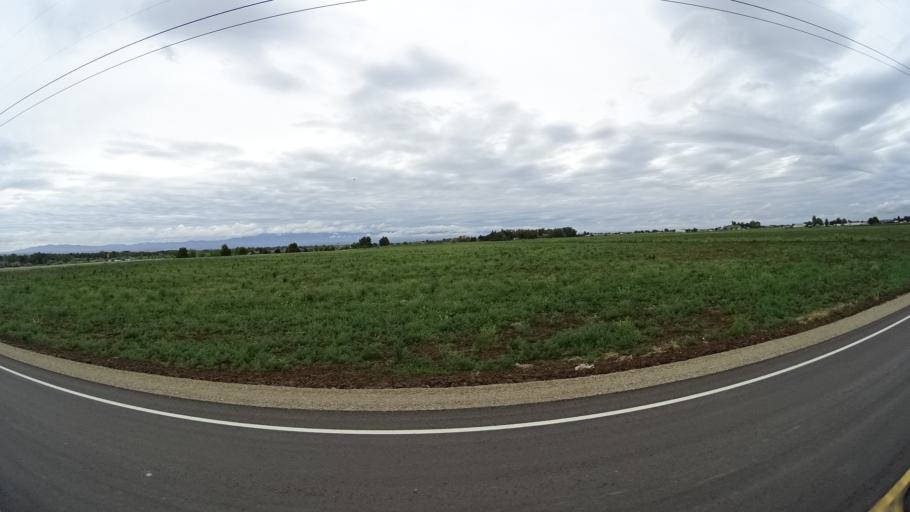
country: US
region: Idaho
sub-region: Ada County
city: Star
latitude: 43.6698
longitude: -116.5128
